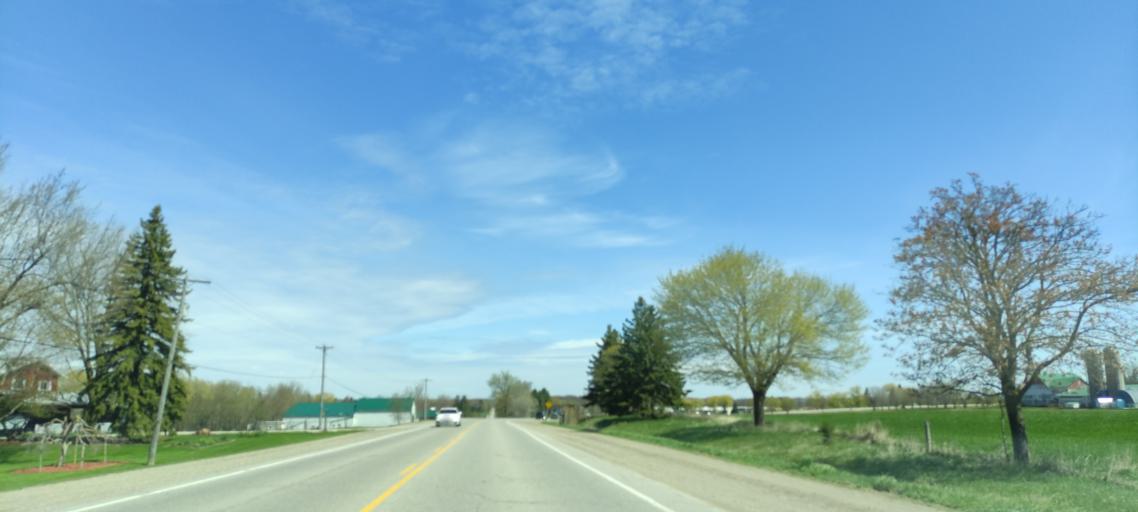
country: CA
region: Ontario
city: Waterloo
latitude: 43.5984
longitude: -80.6065
